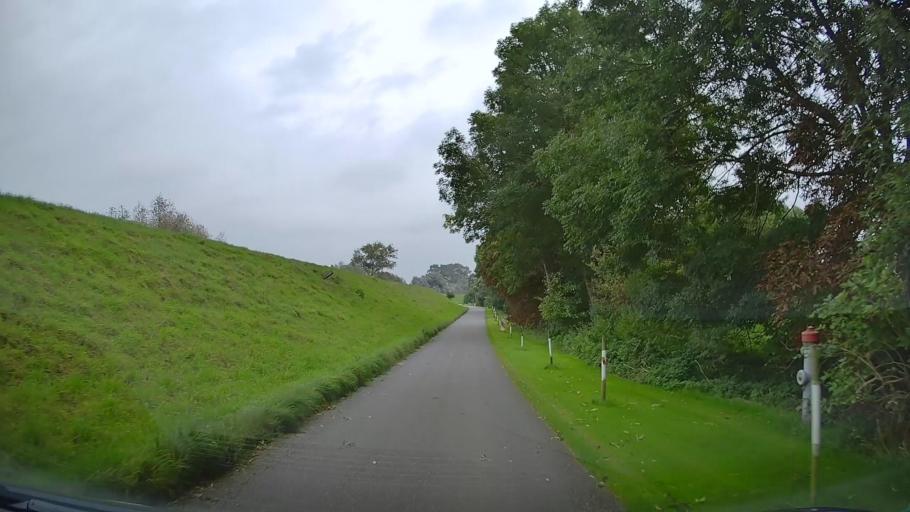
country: DE
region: Lower Saxony
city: Krummendeich
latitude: 53.8328
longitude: 9.1929
